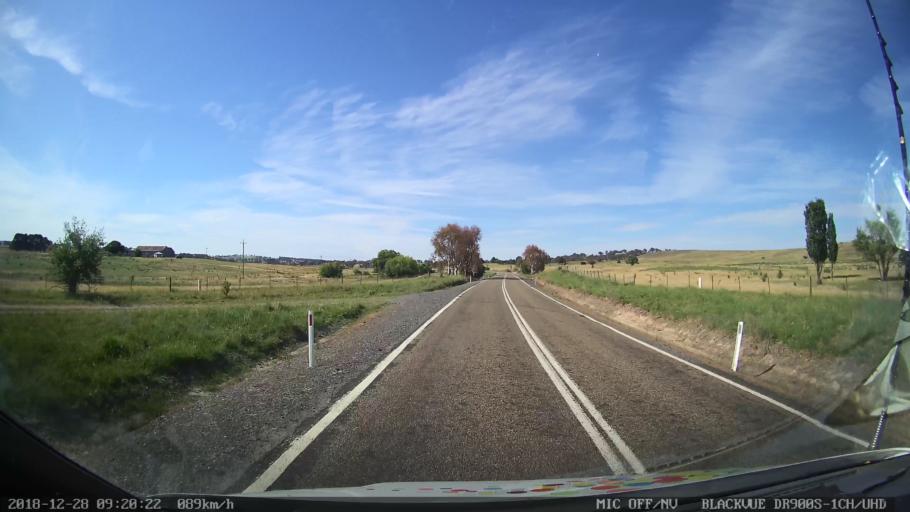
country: AU
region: New South Wales
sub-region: Upper Lachlan Shire
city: Crookwell
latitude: -34.3491
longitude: 149.3722
